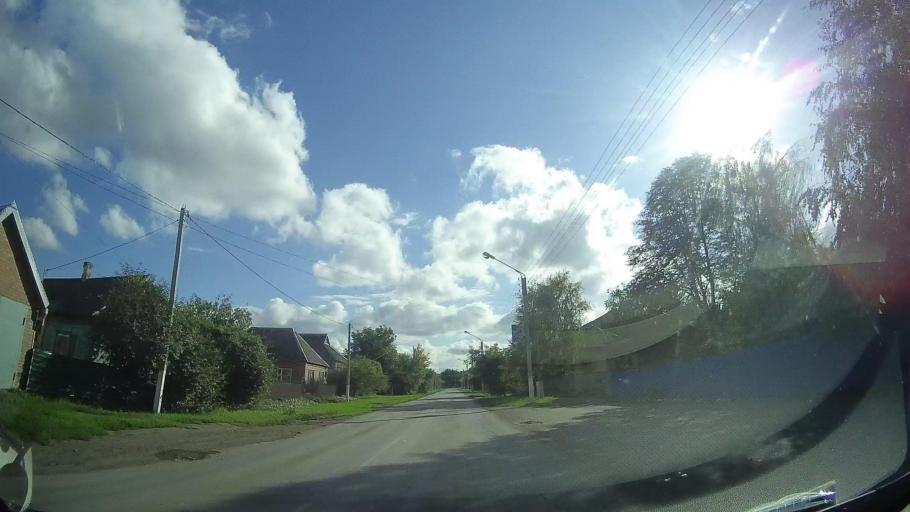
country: RU
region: Rostov
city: Tselina
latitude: 46.5326
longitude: 41.0335
